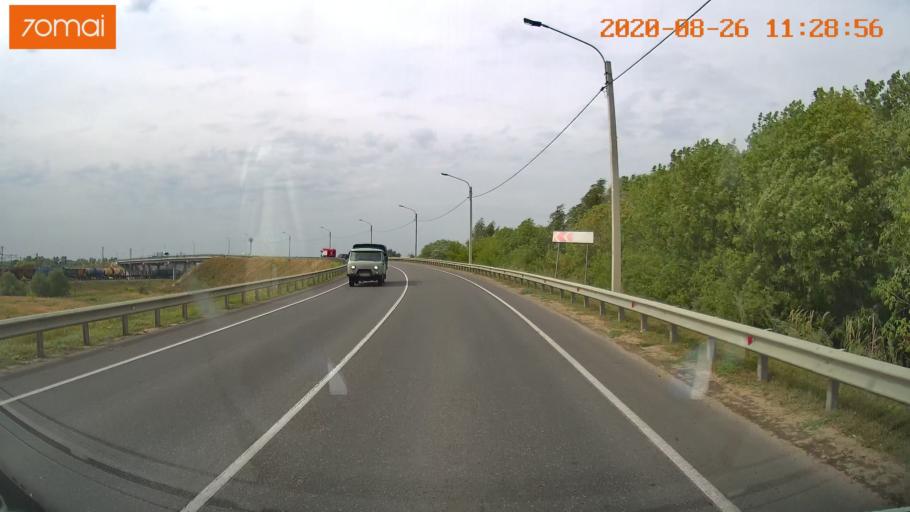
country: RU
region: Rjazan
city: Shilovo
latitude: 54.3235
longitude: 40.9036
